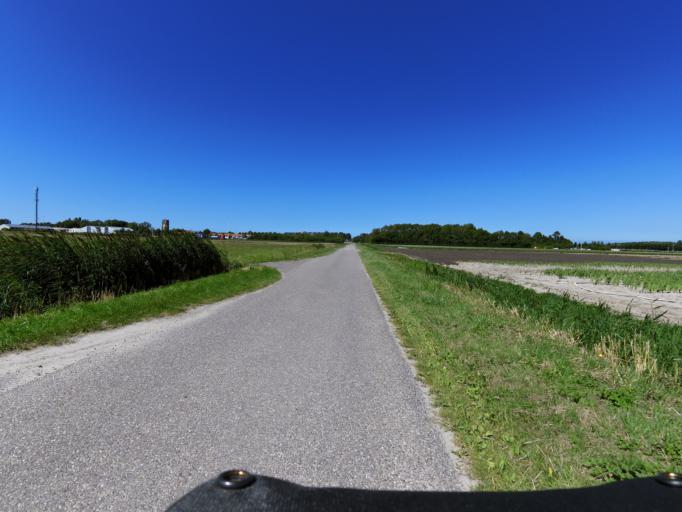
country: NL
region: South Holland
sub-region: Gemeente Goeree-Overflakkee
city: Goedereede
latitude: 51.8124
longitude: 3.9848
